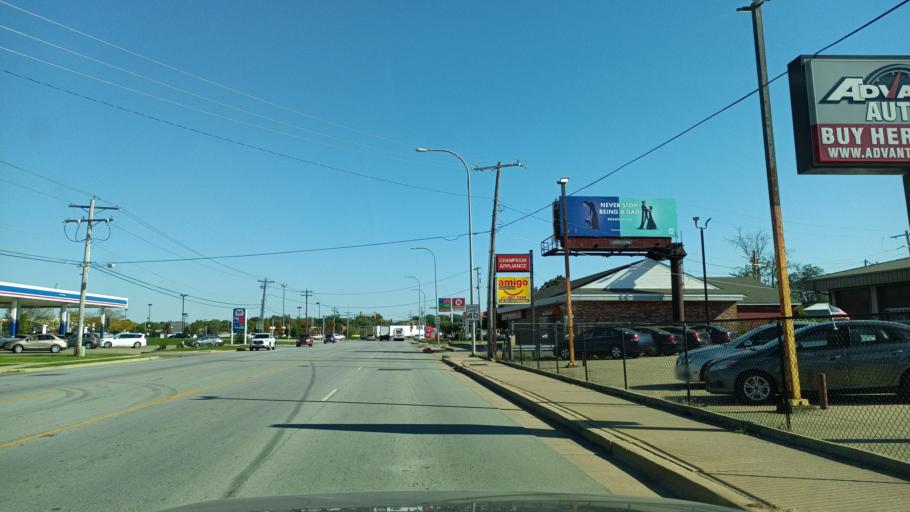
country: US
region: Illinois
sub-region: Champaign County
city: Champaign
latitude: 40.1331
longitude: -88.2602
